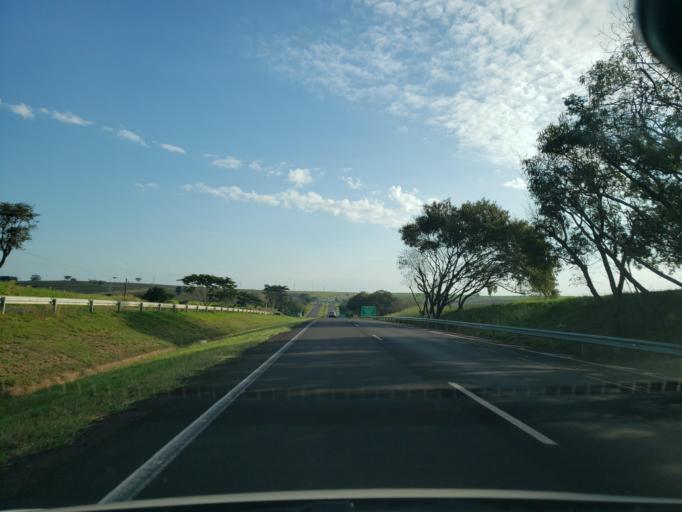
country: BR
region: Sao Paulo
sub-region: Valparaiso
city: Valparaiso
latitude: -21.2122
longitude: -50.8307
